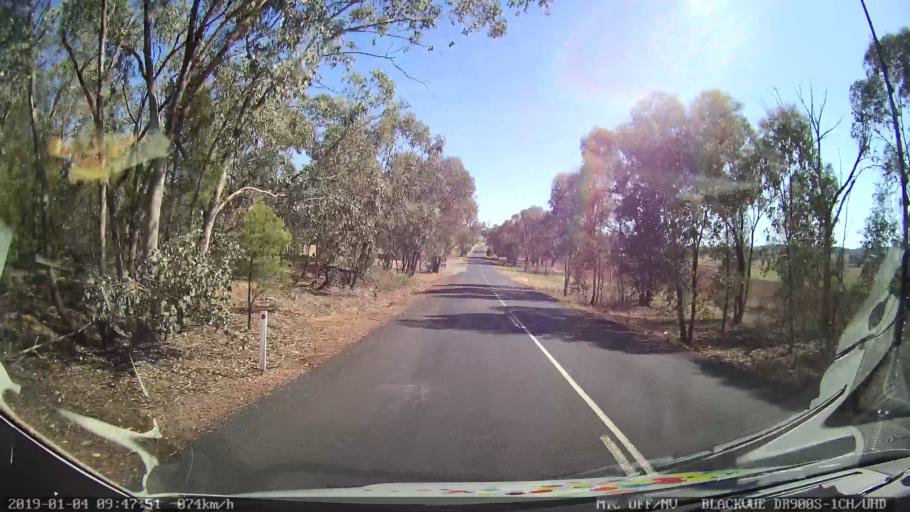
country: AU
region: New South Wales
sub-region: Cabonne
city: Canowindra
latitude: -33.6023
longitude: 148.4318
